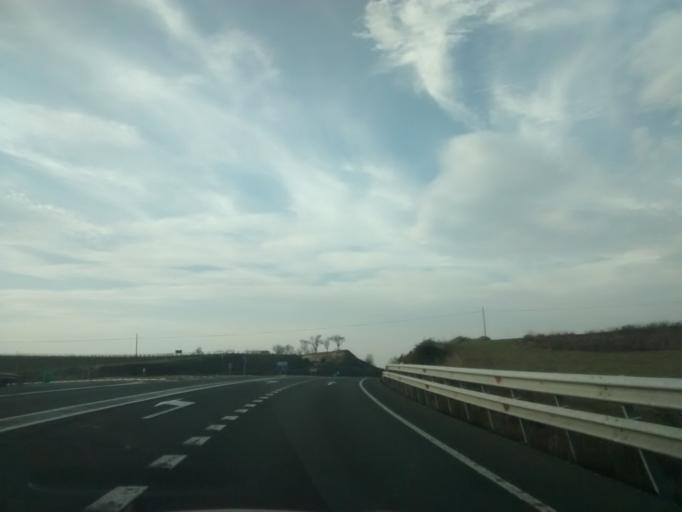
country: ES
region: La Rioja
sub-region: Provincia de La Rioja
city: Ollauri
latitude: 42.5486
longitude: -2.8306
